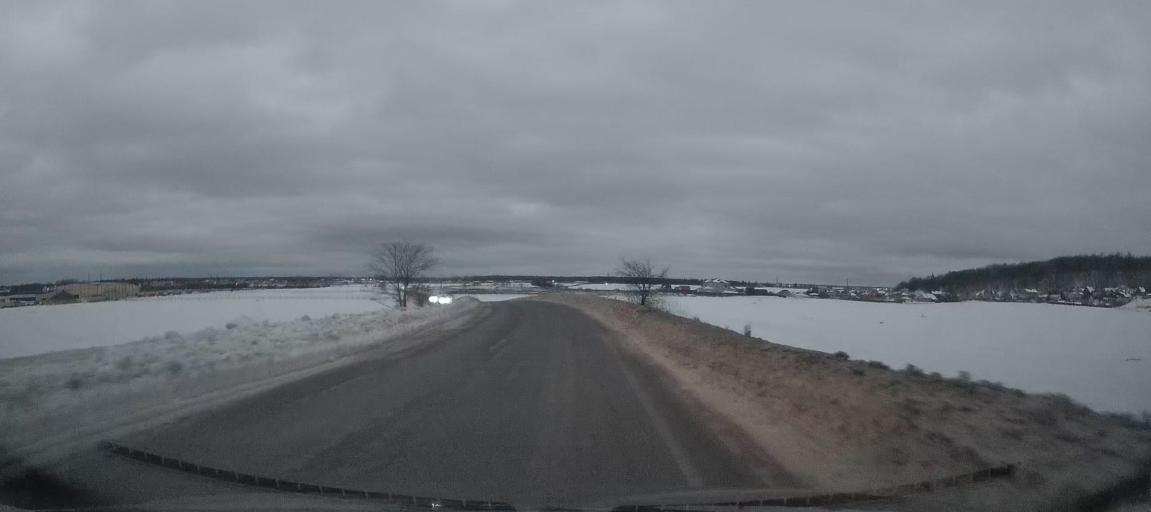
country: RU
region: Leningrad
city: Taytsy
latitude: 59.6919
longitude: 30.1422
